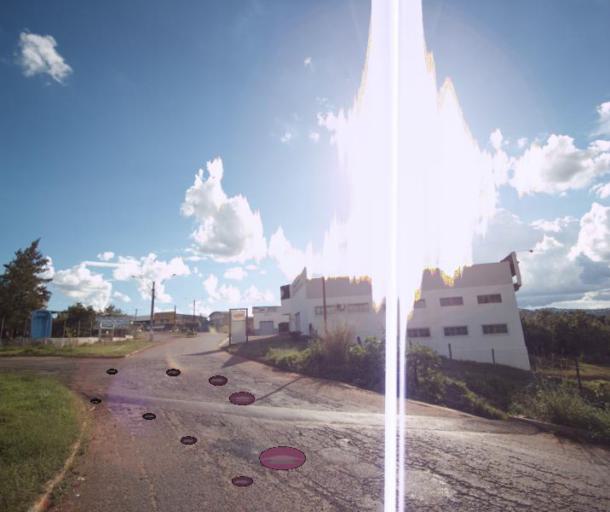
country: BR
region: Goias
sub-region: Rialma
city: Rialma
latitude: -15.3099
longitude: -49.5721
